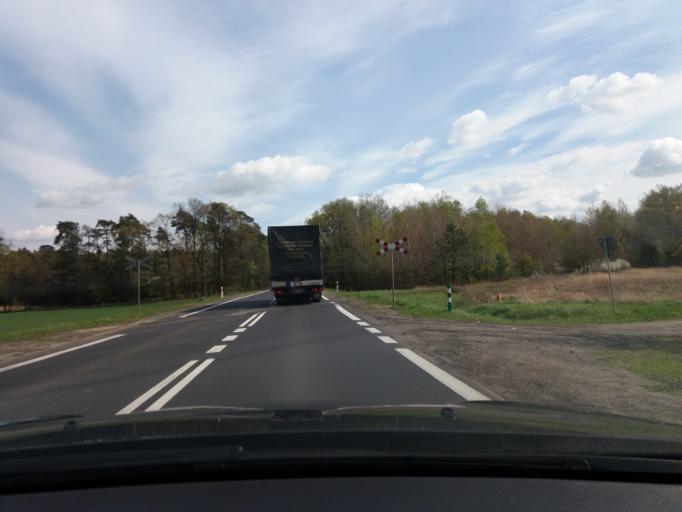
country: PL
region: Lower Silesian Voivodeship
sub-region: Powiat sredzki
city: Malczyce
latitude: 51.1816
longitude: 16.5248
